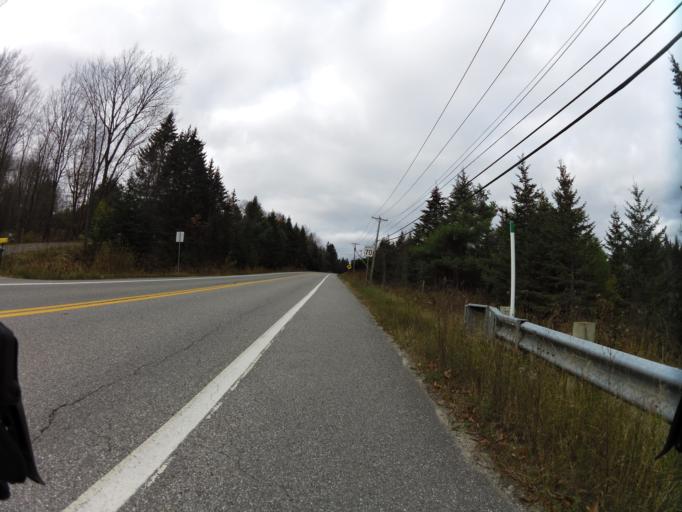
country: CA
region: Quebec
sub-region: Outaouais
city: Wakefield
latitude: 45.5800
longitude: -75.8795
